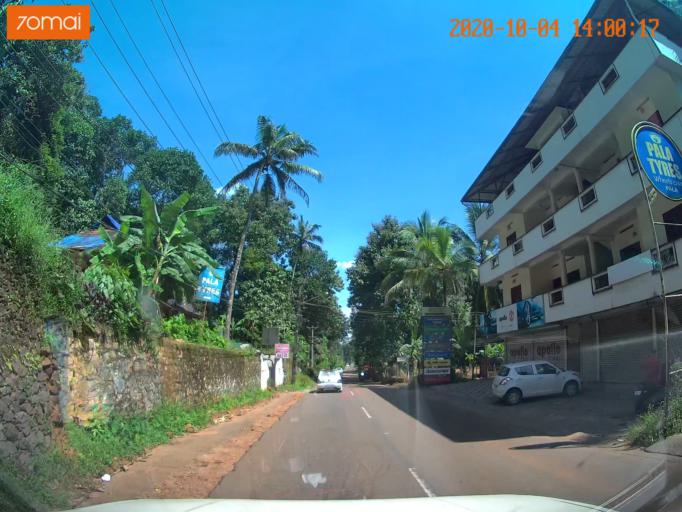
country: IN
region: Kerala
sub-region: Kottayam
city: Lalam
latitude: 9.7136
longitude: 76.6674
